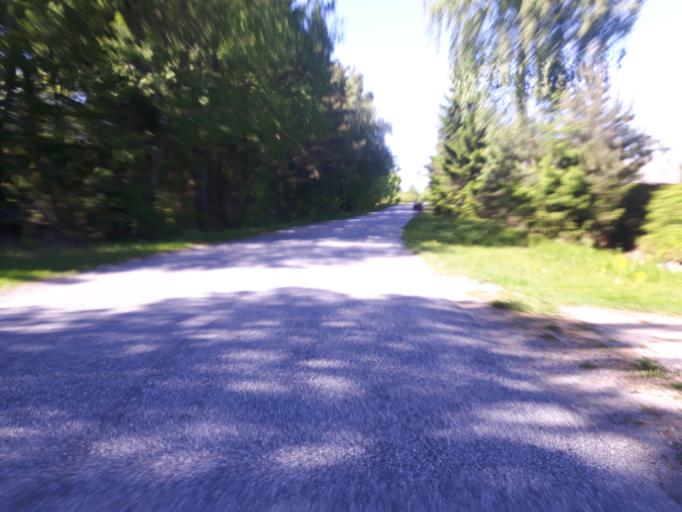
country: EE
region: Laeaene-Virumaa
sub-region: Haljala vald
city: Haljala
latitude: 59.5625
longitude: 26.3111
